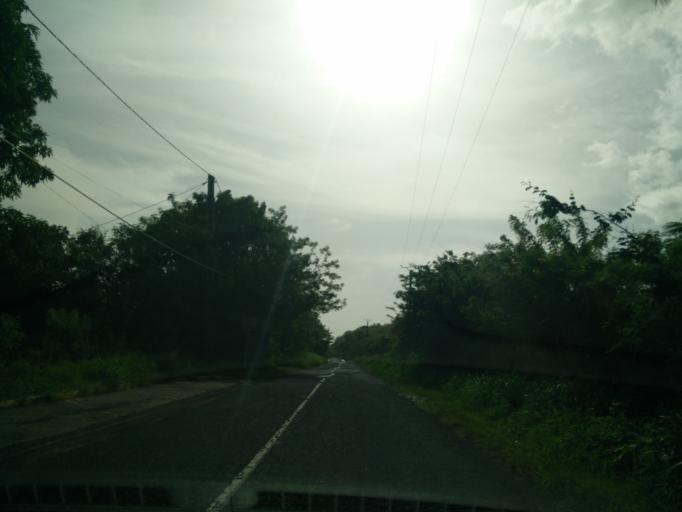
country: MQ
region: Martinique
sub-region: Martinique
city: Saint-Pierre
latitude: 14.7813
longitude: -61.2060
